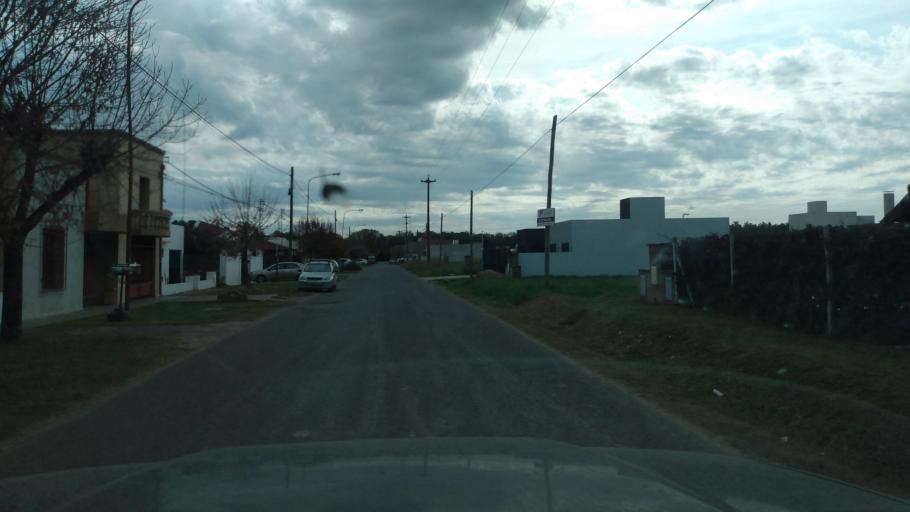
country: AR
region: Buenos Aires
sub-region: Partido de Lujan
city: Lujan
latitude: -34.5949
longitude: -59.1762
